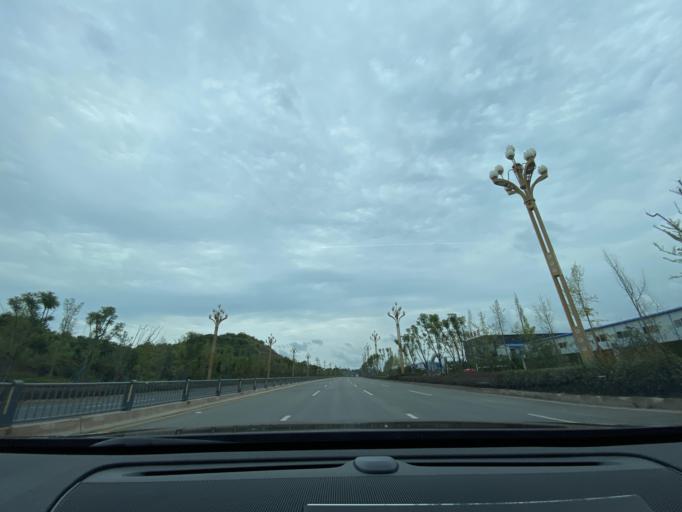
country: CN
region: Sichuan
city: Jiancheng
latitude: 30.4845
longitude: 104.4811
